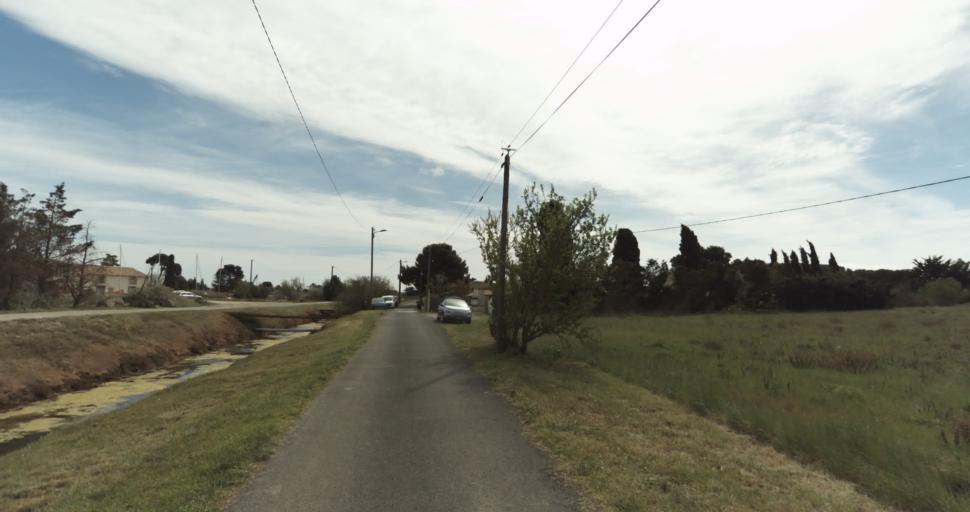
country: FR
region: Languedoc-Roussillon
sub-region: Departement de l'Herault
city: Marseillan
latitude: 43.3378
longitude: 3.5365
